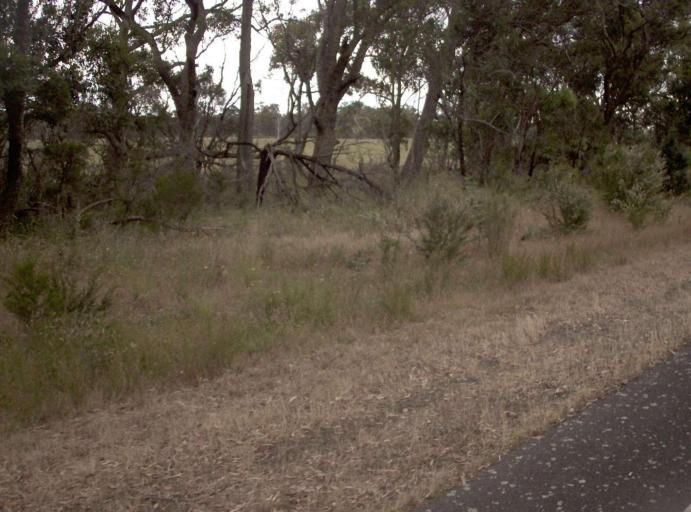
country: AU
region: Victoria
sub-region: Wellington
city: Sale
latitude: -38.4750
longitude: 146.9255
